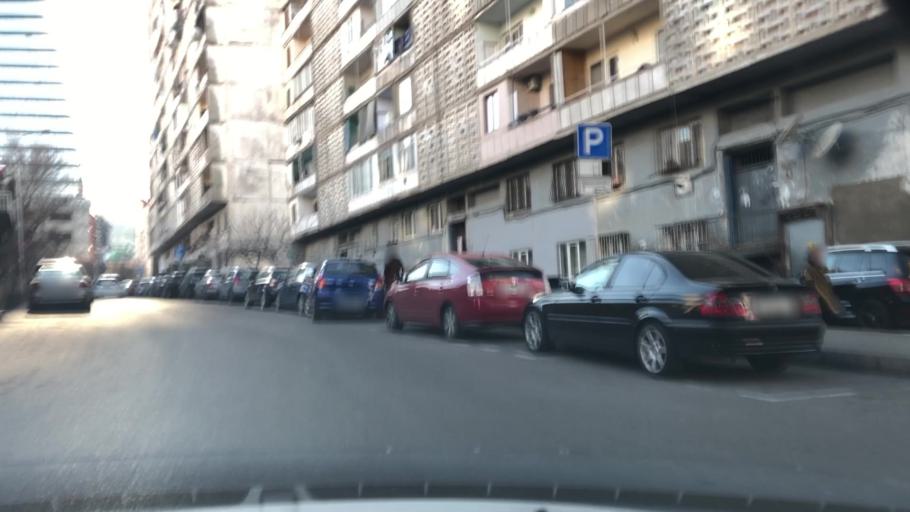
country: GE
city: Tsqnet'i
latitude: 41.7140
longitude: 44.7574
